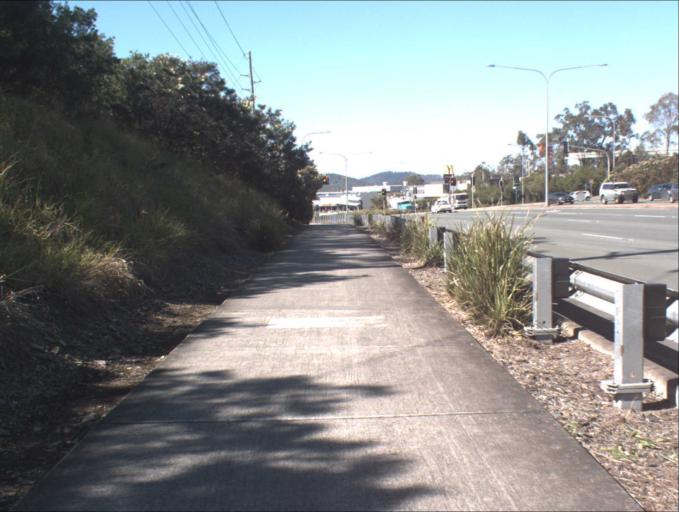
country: AU
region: Queensland
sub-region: Logan
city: Waterford West
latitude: -27.7083
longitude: 153.1610
